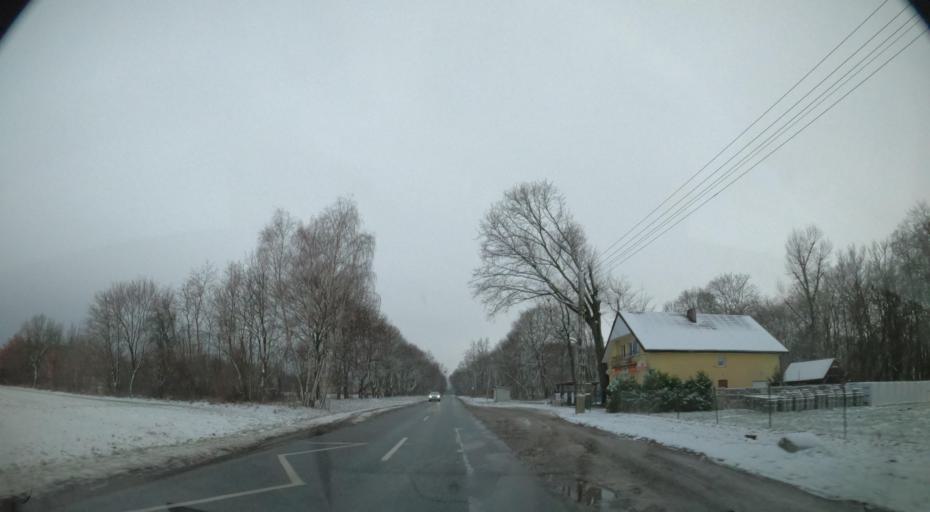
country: PL
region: Kujawsko-Pomorskie
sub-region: Powiat lipnowski
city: Dobrzyn nad Wisla
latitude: 52.6518
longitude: 19.3654
